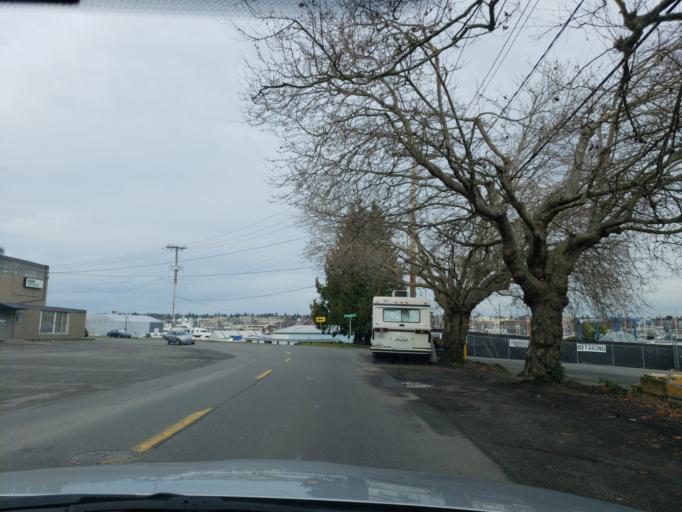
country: US
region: Washington
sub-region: King County
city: Seattle
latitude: 47.6588
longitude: -122.3833
